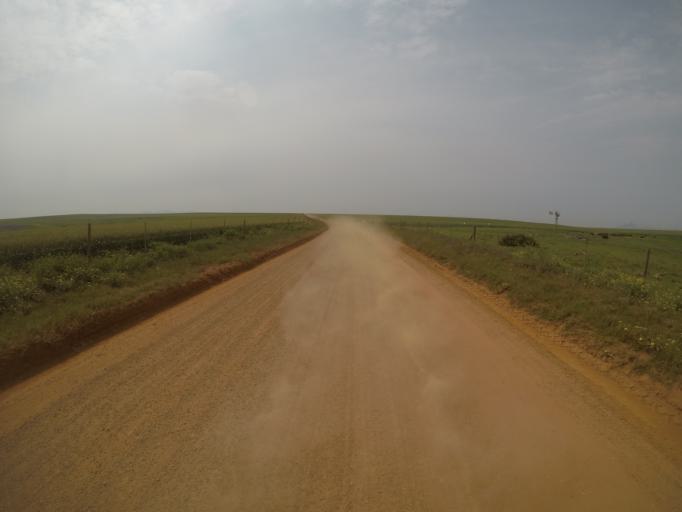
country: ZA
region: Western Cape
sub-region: City of Cape Town
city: Kraaifontein
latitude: -33.7236
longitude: 18.6691
